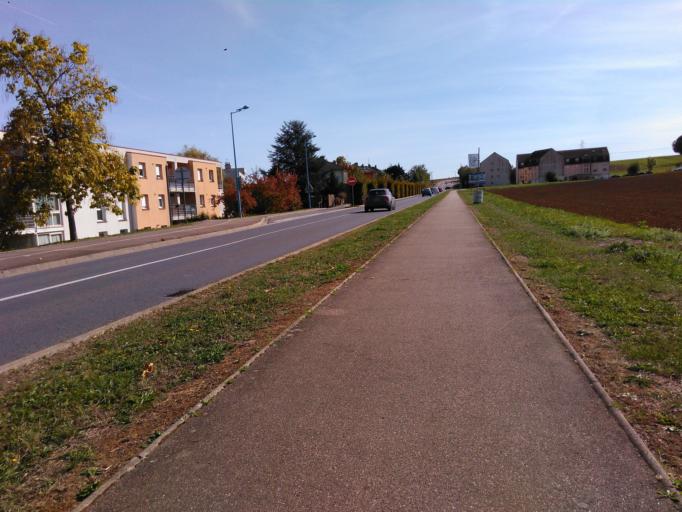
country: FR
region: Lorraine
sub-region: Departement de la Moselle
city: Hettange-Grande
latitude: 49.3958
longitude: 6.1643
